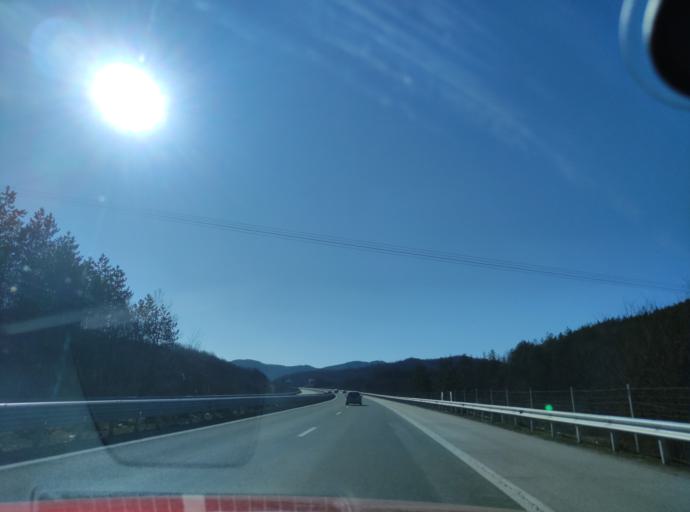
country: BG
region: Sofiya
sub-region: Obshtina Pravets
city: Pravets
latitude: 42.9341
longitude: 23.9506
